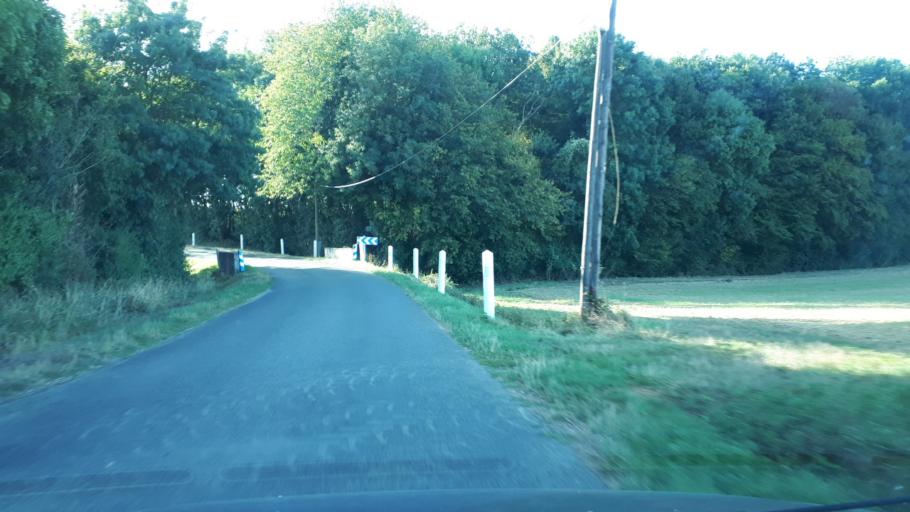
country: FR
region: Centre
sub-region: Departement d'Indre-et-Loire
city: Chateau-Renault
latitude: 47.6605
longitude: 0.9348
